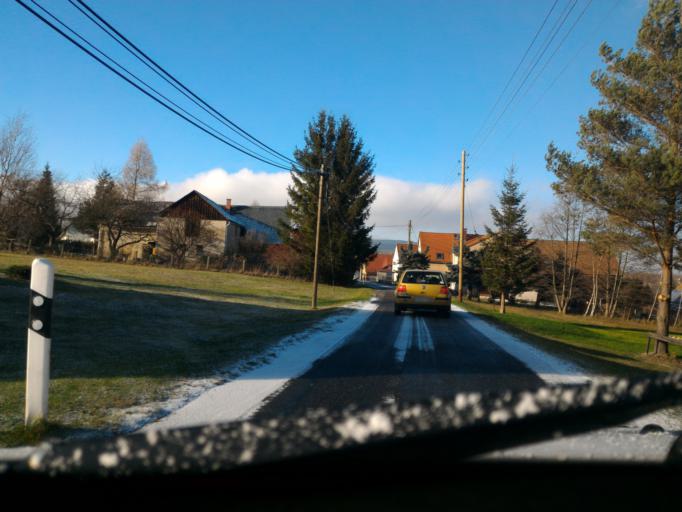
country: CZ
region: Ustecky
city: Varnsdorf
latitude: 50.8792
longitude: 14.6366
